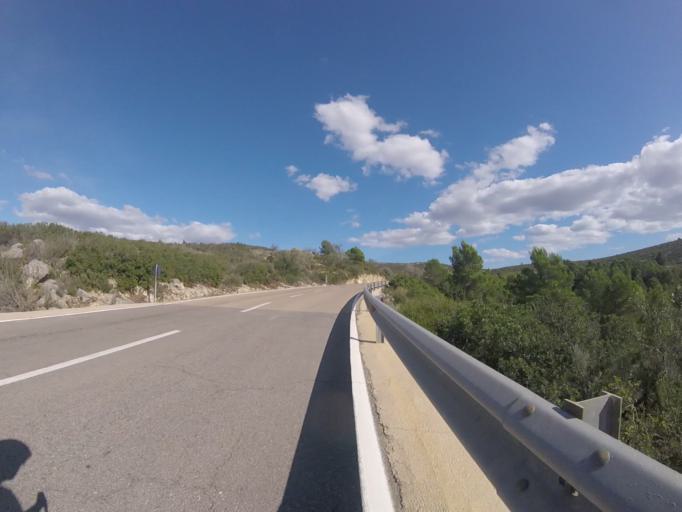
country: ES
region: Valencia
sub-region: Provincia de Castello
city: Cuevas de Vinroma
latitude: 40.2954
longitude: 0.1743
